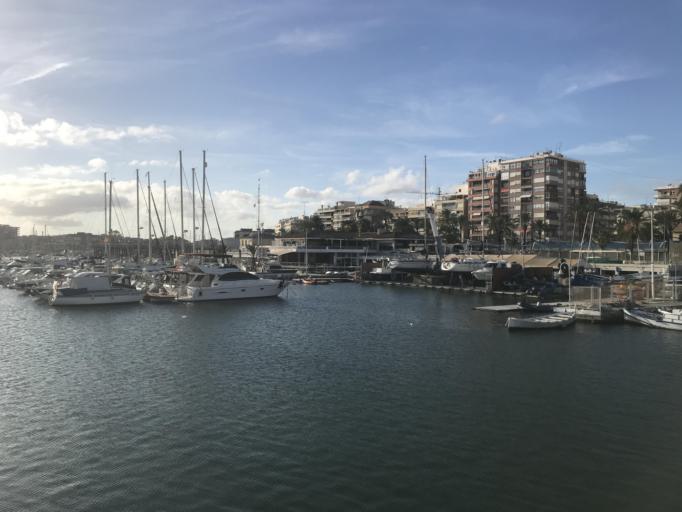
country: ES
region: Valencia
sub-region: Provincia de Alicante
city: Torrevieja
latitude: 37.9743
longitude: -0.6814
